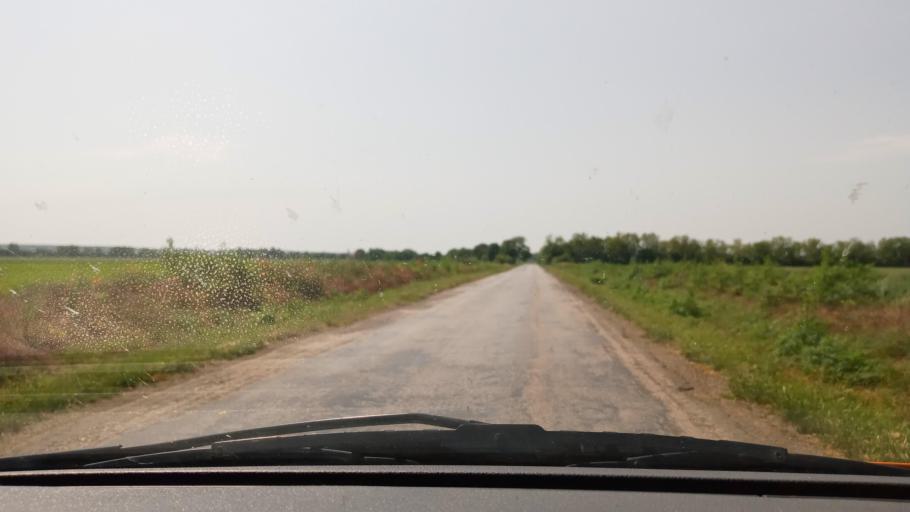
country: HU
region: Baranya
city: Szentlorinc
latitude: 46.0222
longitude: 18.0322
